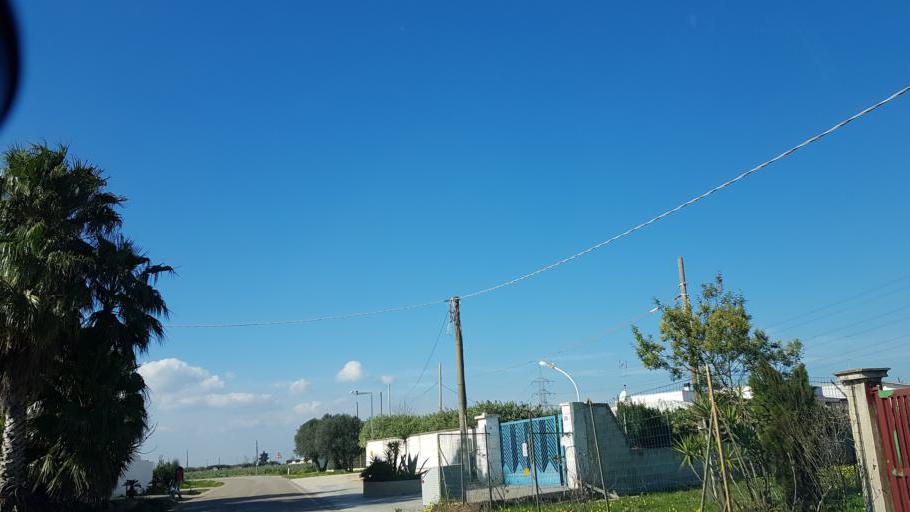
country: IT
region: Apulia
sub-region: Provincia di Brindisi
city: La Rosa
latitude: 40.5915
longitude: 17.9404
